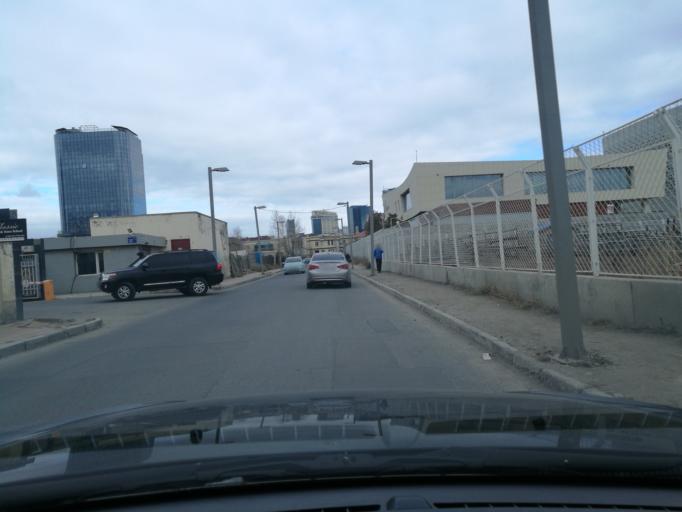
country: MN
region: Ulaanbaatar
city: Ulaanbaatar
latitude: 47.9029
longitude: 106.9207
